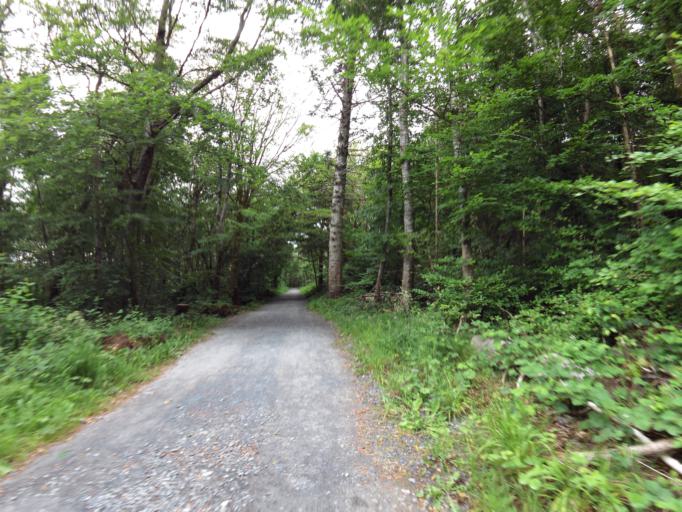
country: IE
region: Connaught
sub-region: County Galway
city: Gort
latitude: 53.0898
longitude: -8.8443
